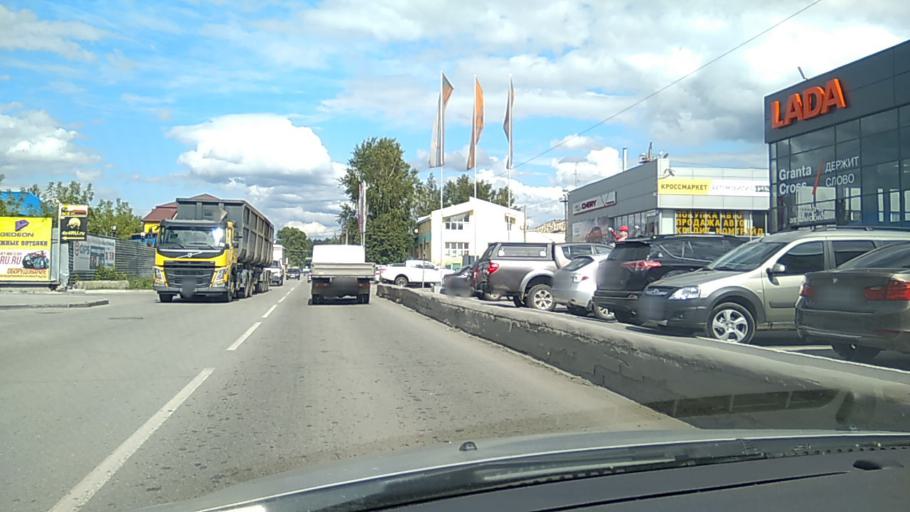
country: RU
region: Sverdlovsk
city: Shuvakish
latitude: 56.8853
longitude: 60.5338
